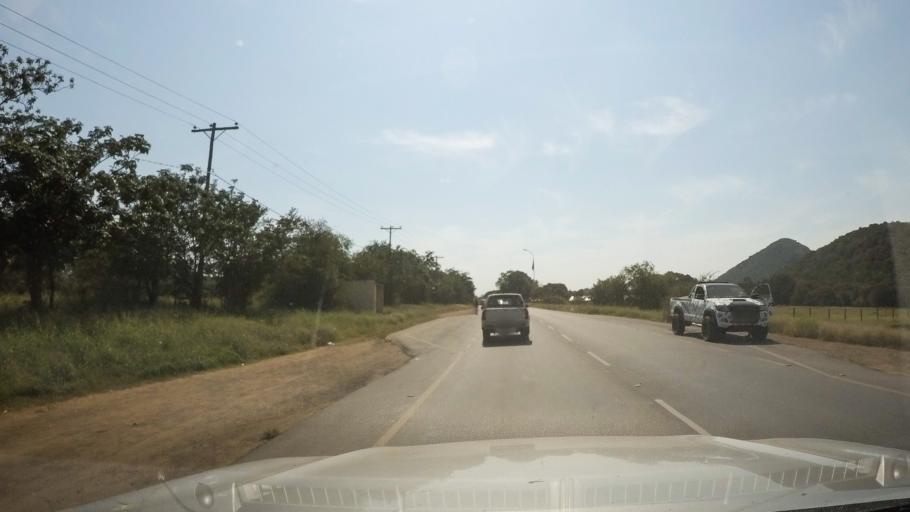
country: BW
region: South East
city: Lobatse
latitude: -25.2214
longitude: 25.6794
